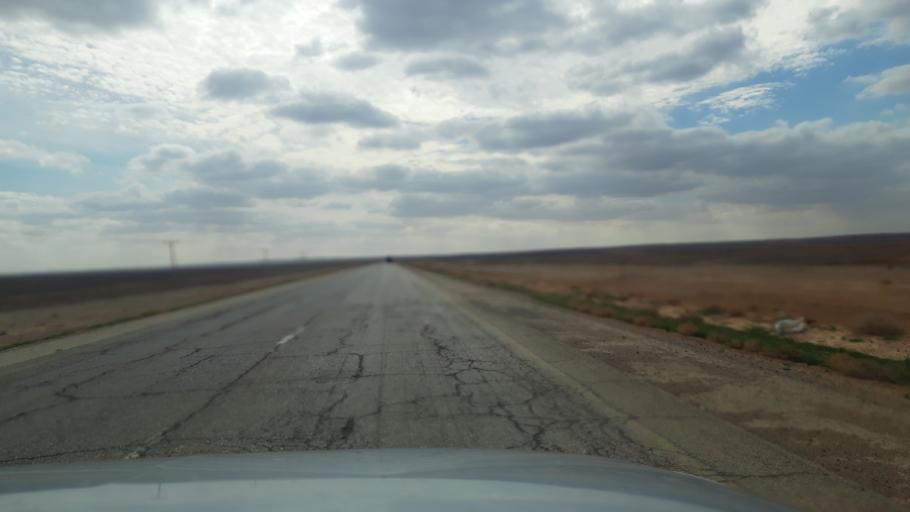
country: JO
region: Amman
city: Al Azraq ash Shamali
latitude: 31.8273
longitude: 36.6174
